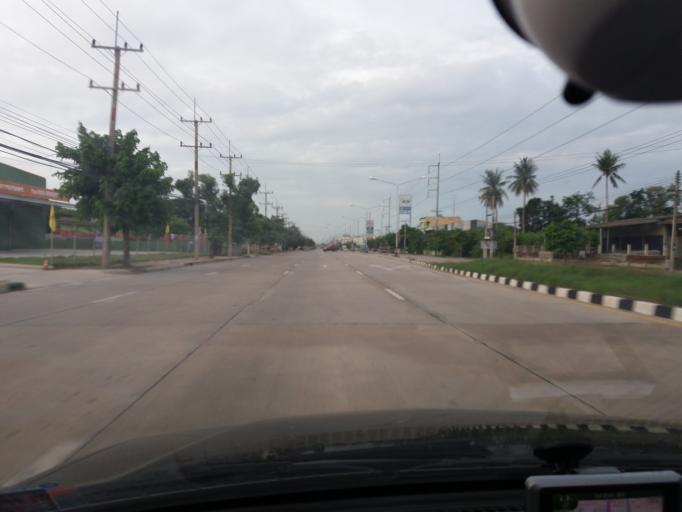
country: TH
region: Suphan Buri
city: U Thong
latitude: 14.3892
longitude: 99.8952
